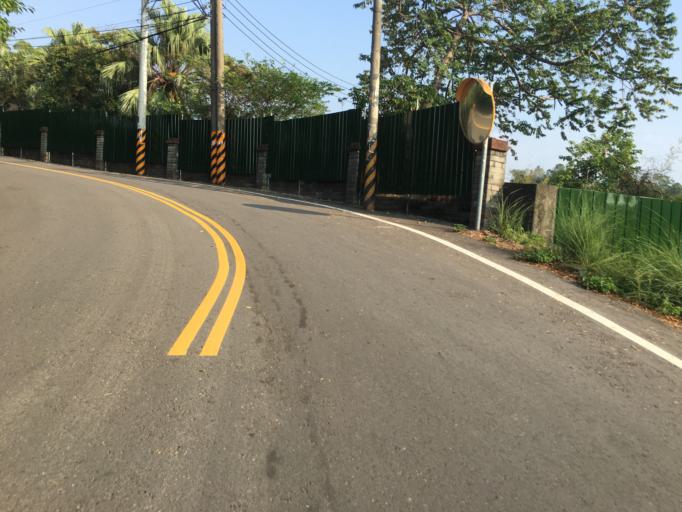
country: TW
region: Taiwan
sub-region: Hsinchu
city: Hsinchu
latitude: 24.7478
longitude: 121.0356
